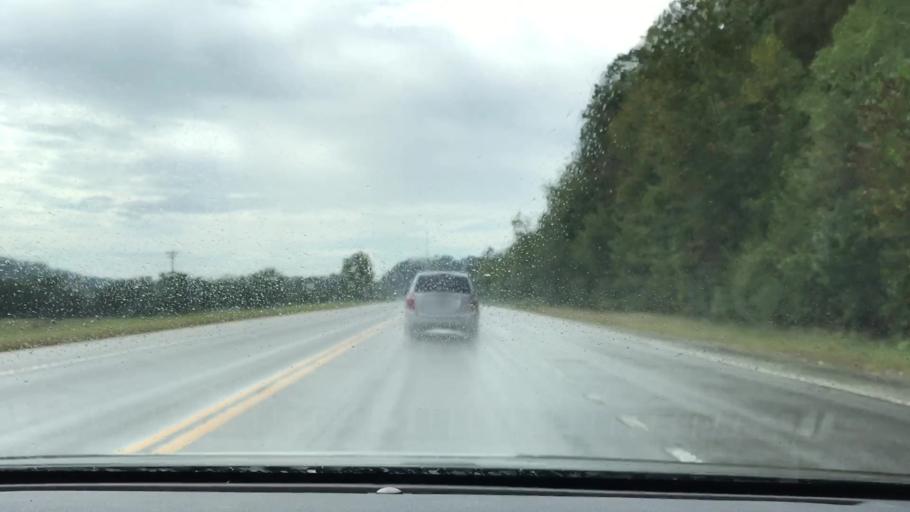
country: US
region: Tennessee
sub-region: Smith County
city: Carthage
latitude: 36.2526
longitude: -85.9364
